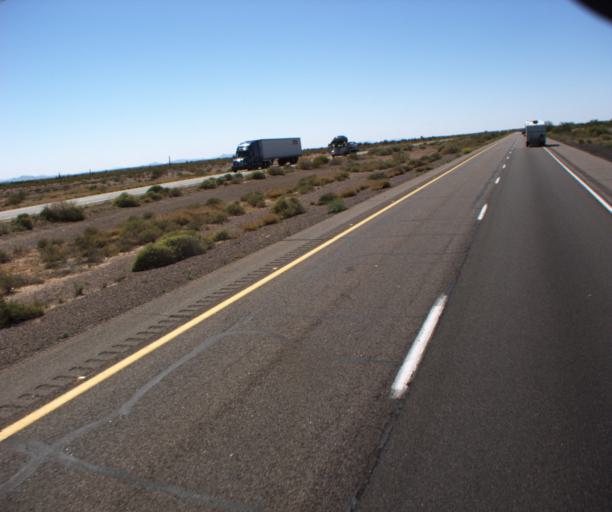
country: US
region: Arizona
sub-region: Maricopa County
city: Gila Bend
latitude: 32.8974
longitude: -113.0233
